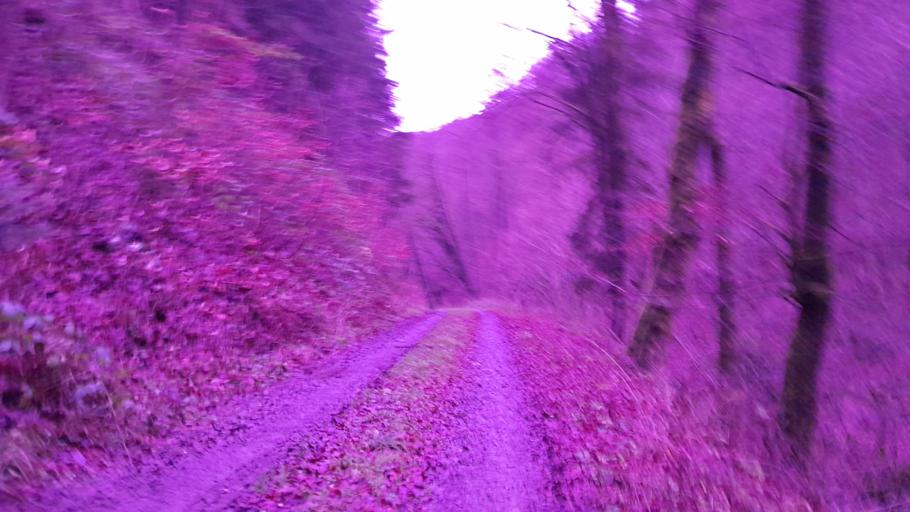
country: DE
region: Rheinland-Pfalz
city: Dasburg
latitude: 50.0770
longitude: 6.1040
